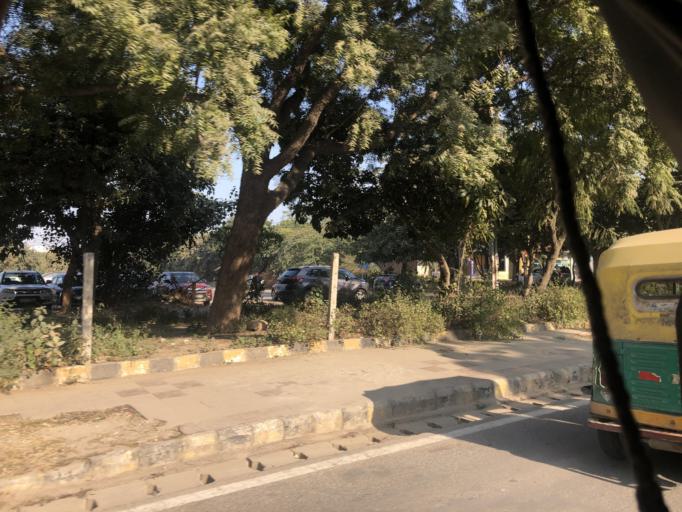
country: IN
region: Haryana
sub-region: Gurgaon
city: Gurgaon
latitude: 28.4632
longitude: 77.0652
